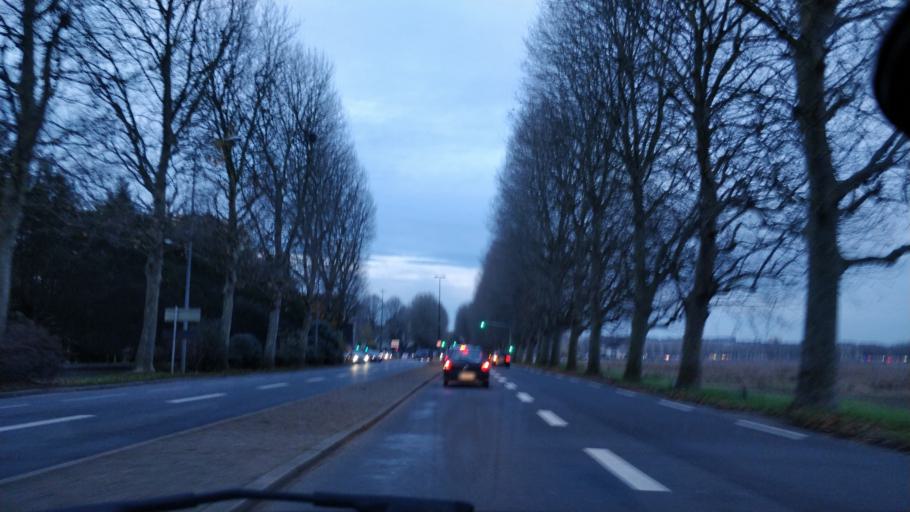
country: FR
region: Lower Normandy
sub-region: Departement du Calvados
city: Caen
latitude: 49.1743
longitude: -0.3722
